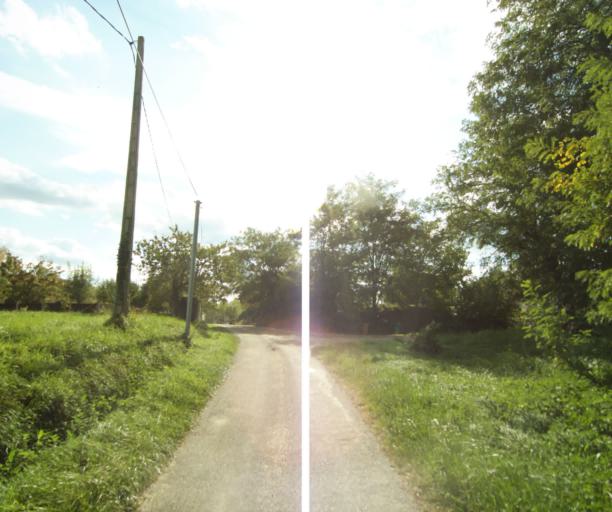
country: FR
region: Midi-Pyrenees
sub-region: Departement du Gers
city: Cazaubon
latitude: 43.9275
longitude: -0.0396
